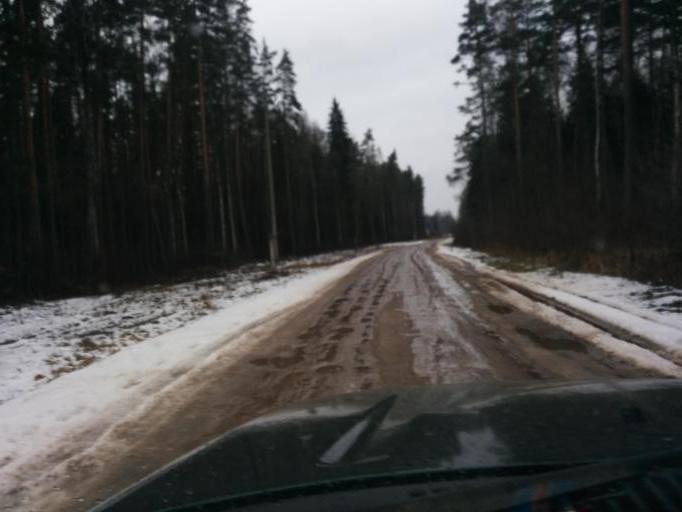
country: LV
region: Ozolnieku
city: Ozolnieki
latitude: 56.6815
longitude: 23.7608
